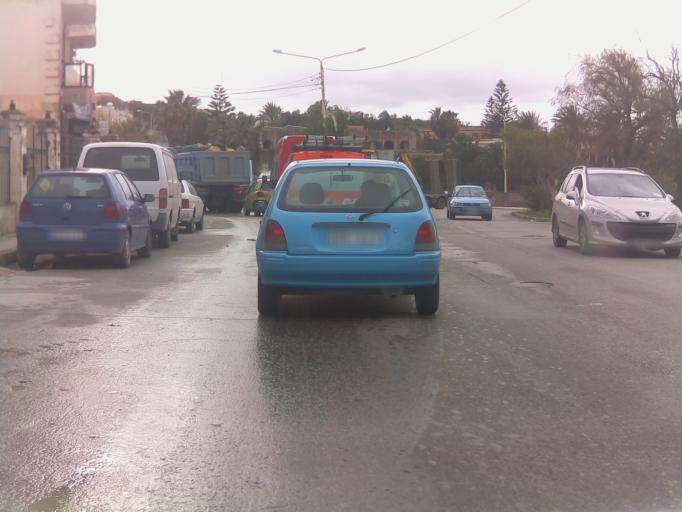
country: MT
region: Il-Mosta
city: Mosta
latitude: 35.9171
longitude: 14.4184
